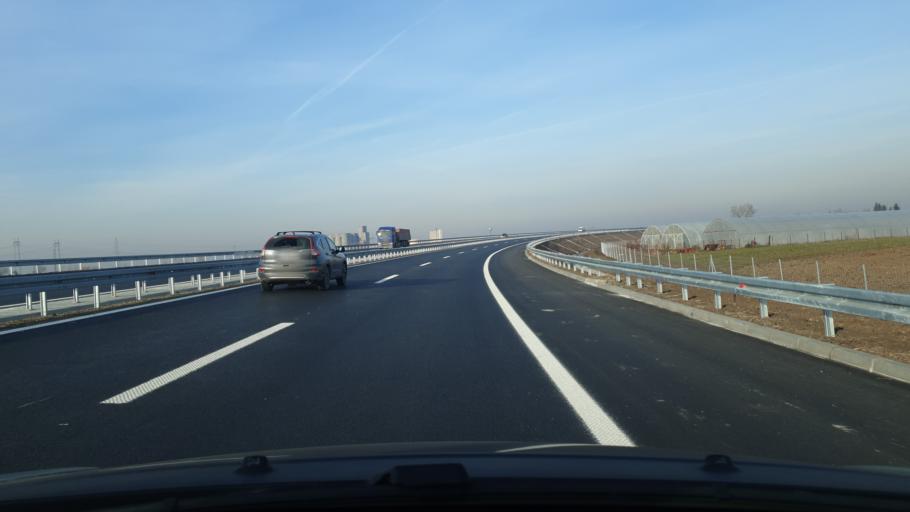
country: RS
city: Boljevci
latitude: 44.7610
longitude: 20.2457
